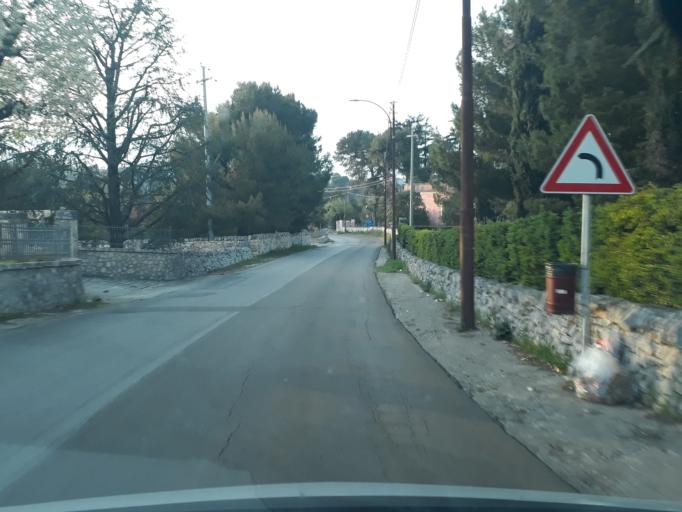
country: IT
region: Apulia
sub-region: Provincia di Brindisi
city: Lamie di Olimpie-Selva
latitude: 40.7981
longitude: 17.3542
